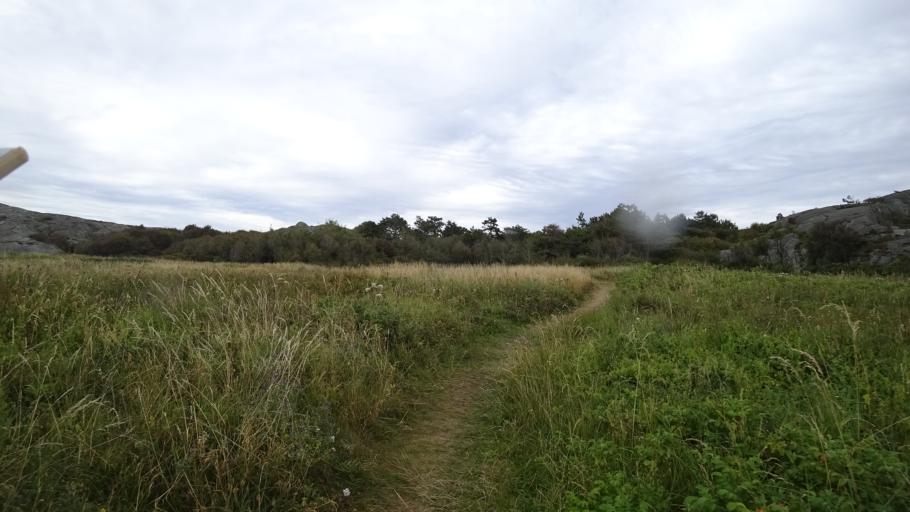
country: SE
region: Vaestra Goetaland
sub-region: Ockero Kommun
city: Hono
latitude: 57.7005
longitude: 11.6195
